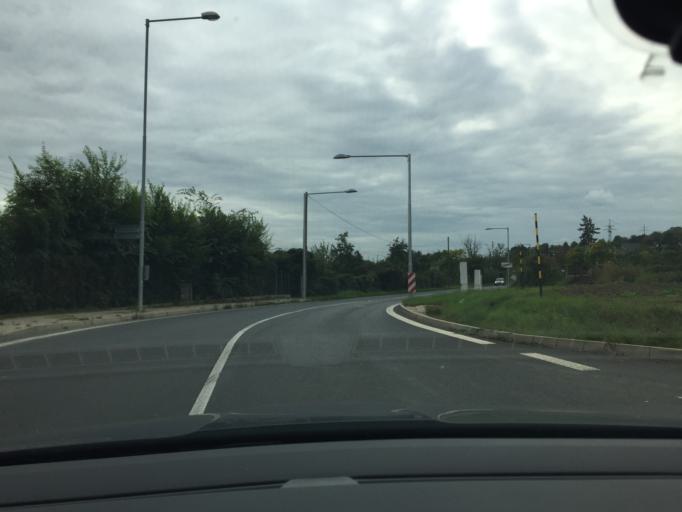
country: CZ
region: Ustecky
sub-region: Okres Litomerice
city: Litomerice
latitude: 50.5310
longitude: 14.1103
